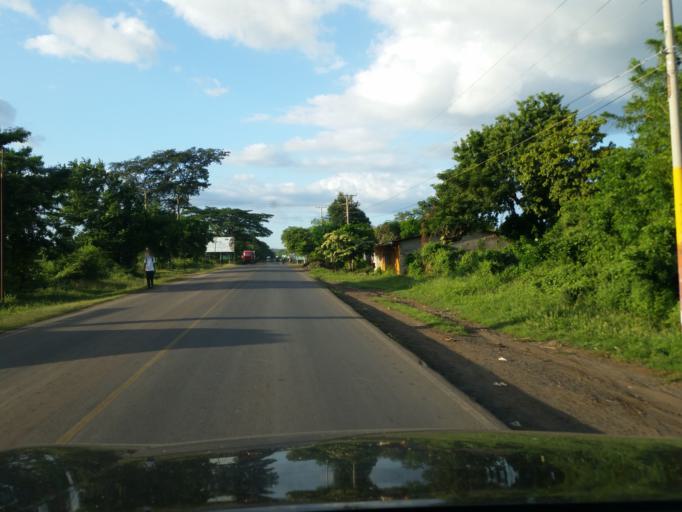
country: NI
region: Granada
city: Nandaime
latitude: 11.7630
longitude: -86.0481
